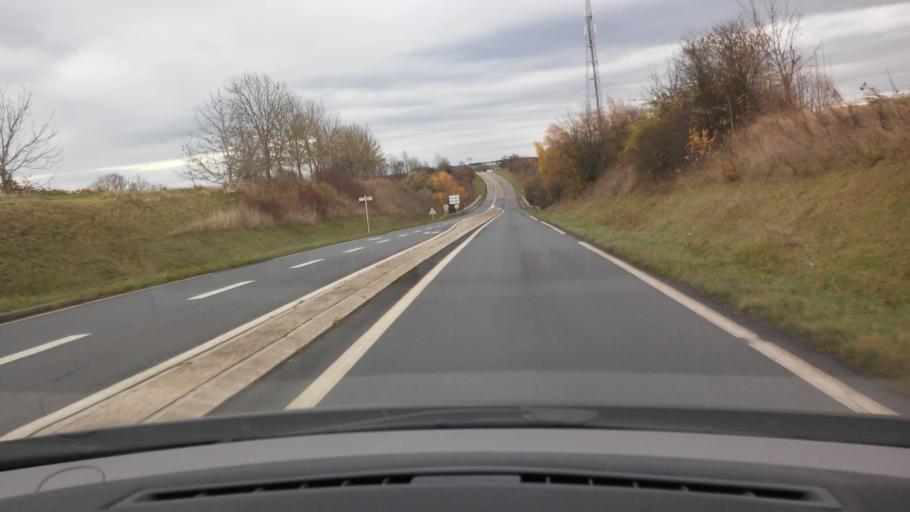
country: FR
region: Lorraine
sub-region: Departement de la Moselle
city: Saint-Julien-les-Metz
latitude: 49.1488
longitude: 6.2474
